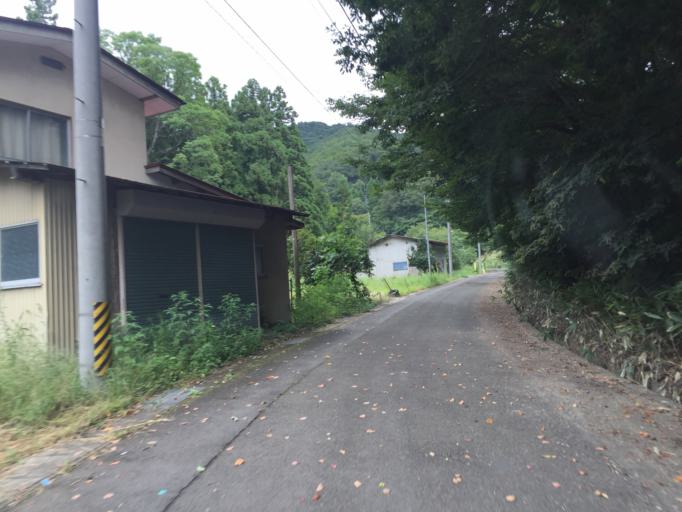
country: JP
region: Fukushima
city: Fukushima-shi
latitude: 37.8347
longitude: 140.3824
